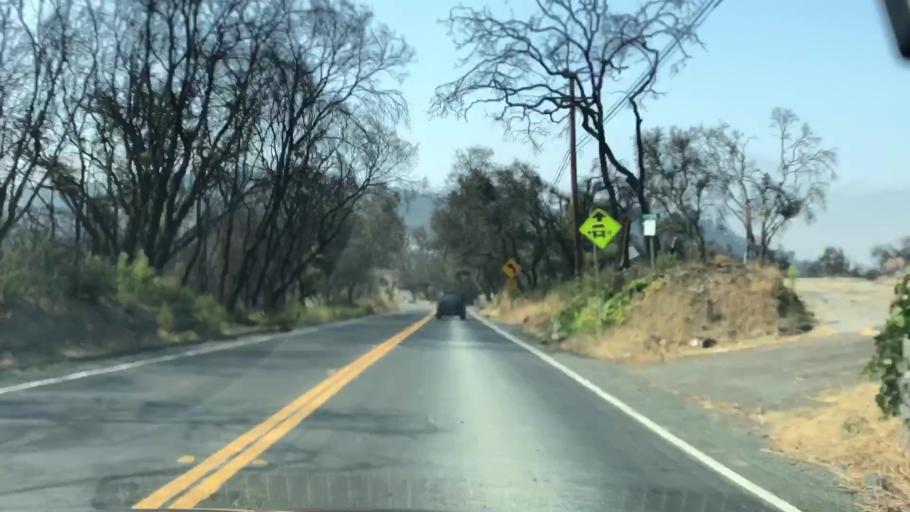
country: US
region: California
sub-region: Sonoma County
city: Larkfield-Wikiup
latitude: 38.5133
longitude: -122.7190
